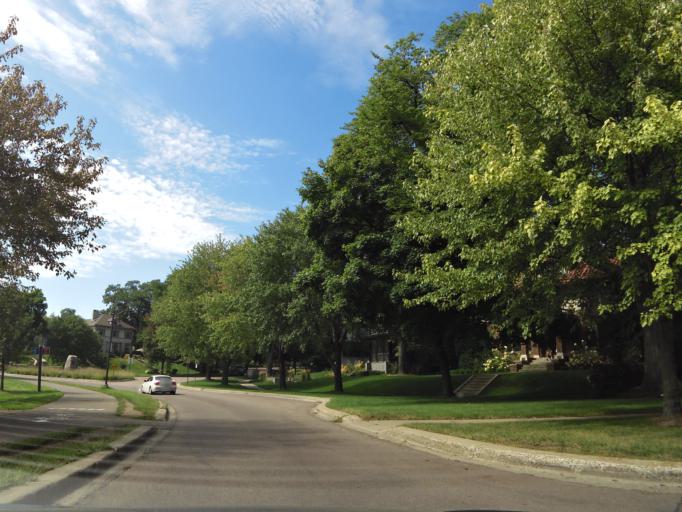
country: US
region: Minnesota
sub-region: Hennepin County
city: Saint Louis Park
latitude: 44.9596
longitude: -93.3086
